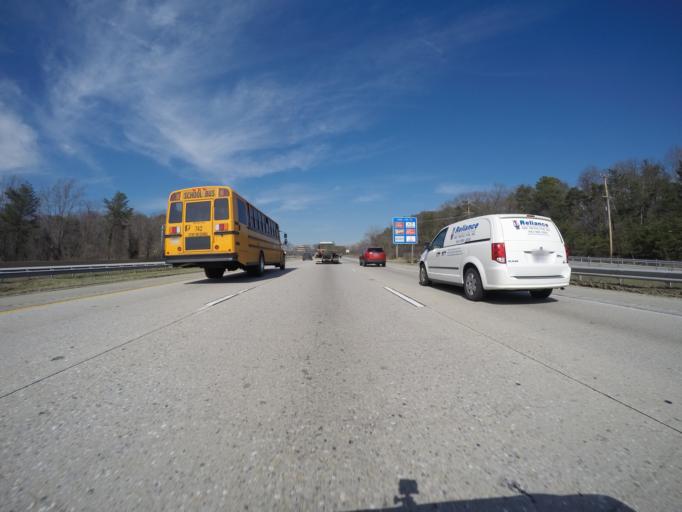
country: US
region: Maryland
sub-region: Anne Arundel County
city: Gambrills
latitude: 39.0812
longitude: -76.6265
